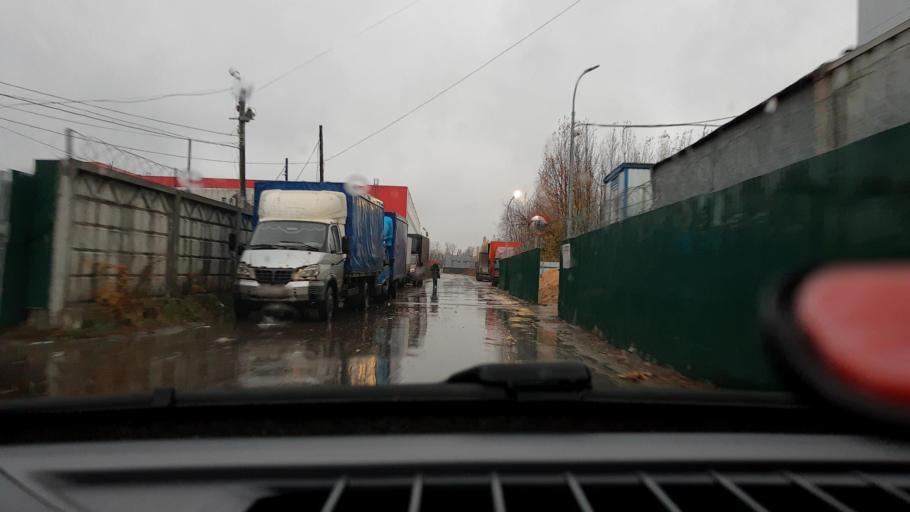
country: RU
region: Nizjnij Novgorod
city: Gorbatovka
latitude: 56.3185
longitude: 43.8519
